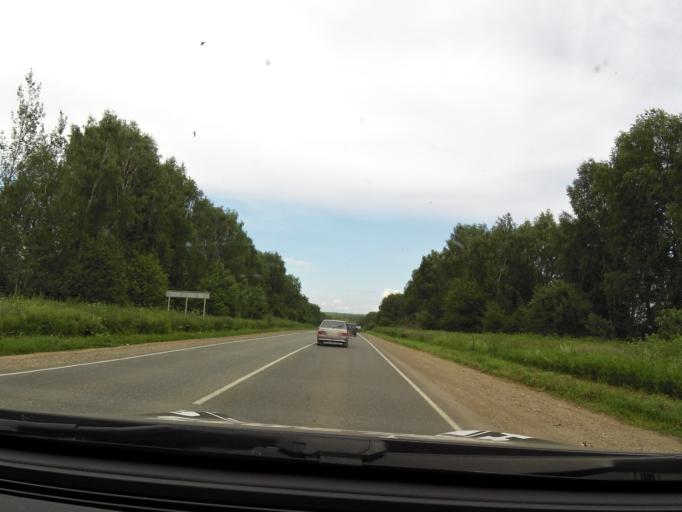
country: RU
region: Kirov
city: Vakhrushi
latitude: 58.6479
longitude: 49.8639
